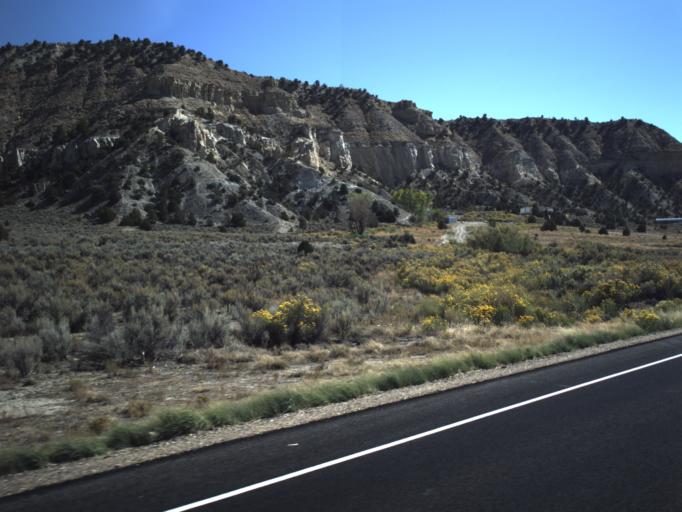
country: US
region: Utah
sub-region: Garfield County
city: Panguitch
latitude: 37.5687
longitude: -111.9897
